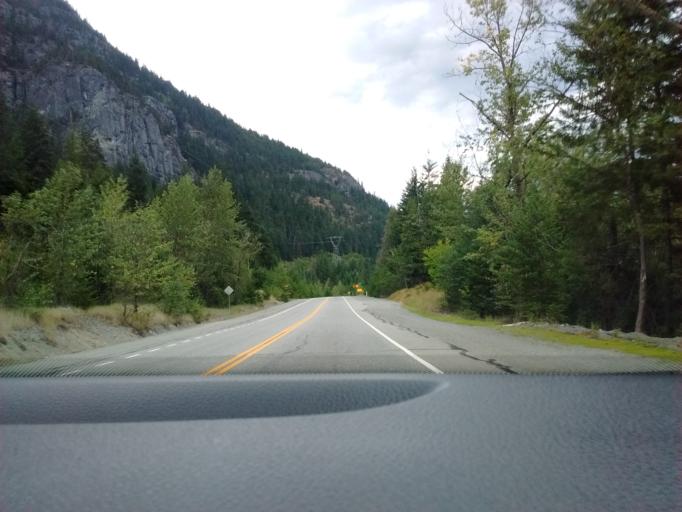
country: CA
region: British Columbia
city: Pemberton
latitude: 50.2908
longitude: -122.8349
